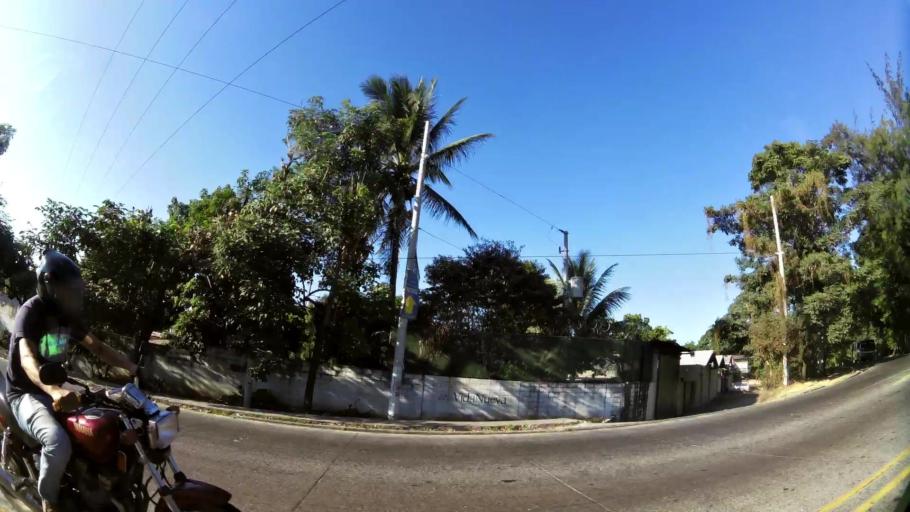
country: SV
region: La Libertad
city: Santa Tecla
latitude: 13.7210
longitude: -89.3578
